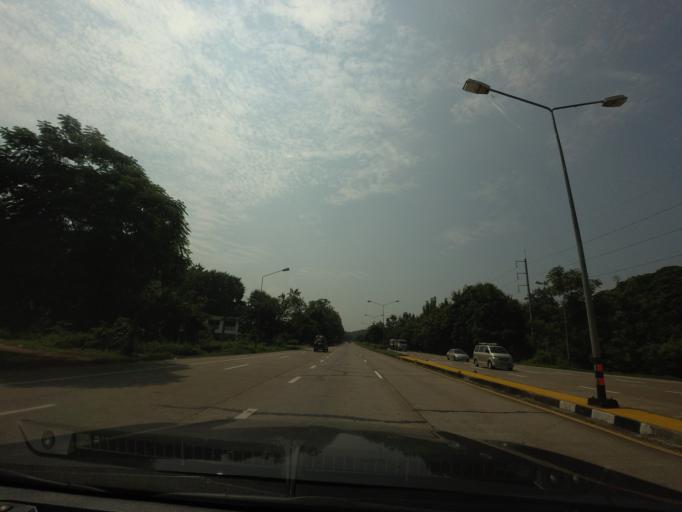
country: TH
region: Phrae
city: Sung Men
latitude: 18.0037
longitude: 100.1041
